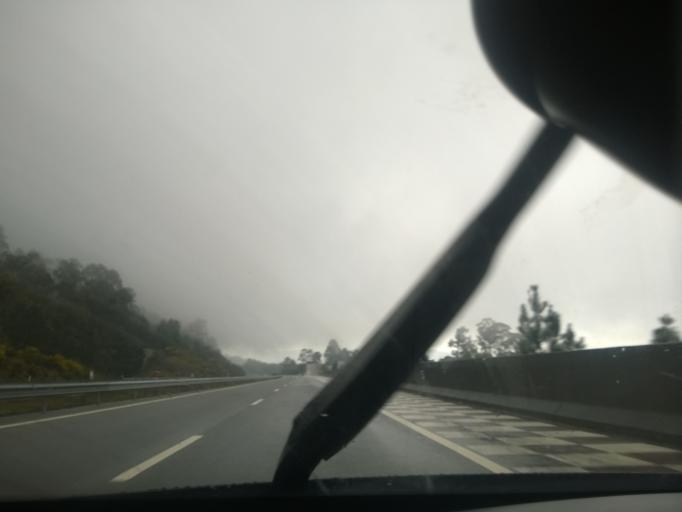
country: PT
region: Braga
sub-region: Fafe
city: Fafe
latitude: 41.4402
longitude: -8.1208
